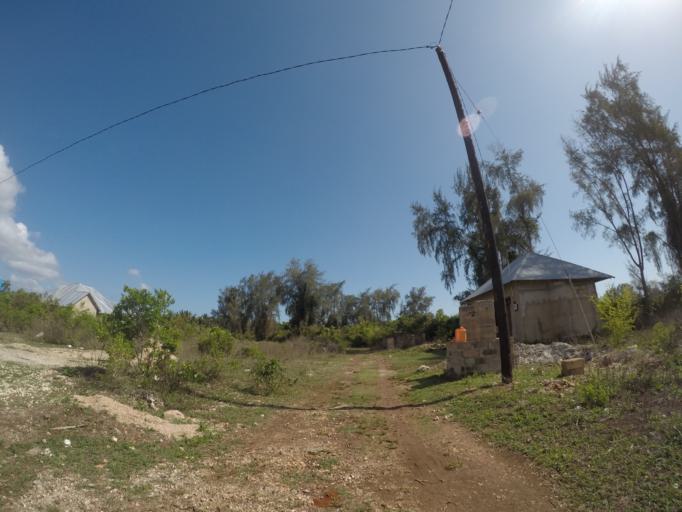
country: TZ
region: Zanzibar Central/South
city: Koani
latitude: -6.2154
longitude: 39.3012
